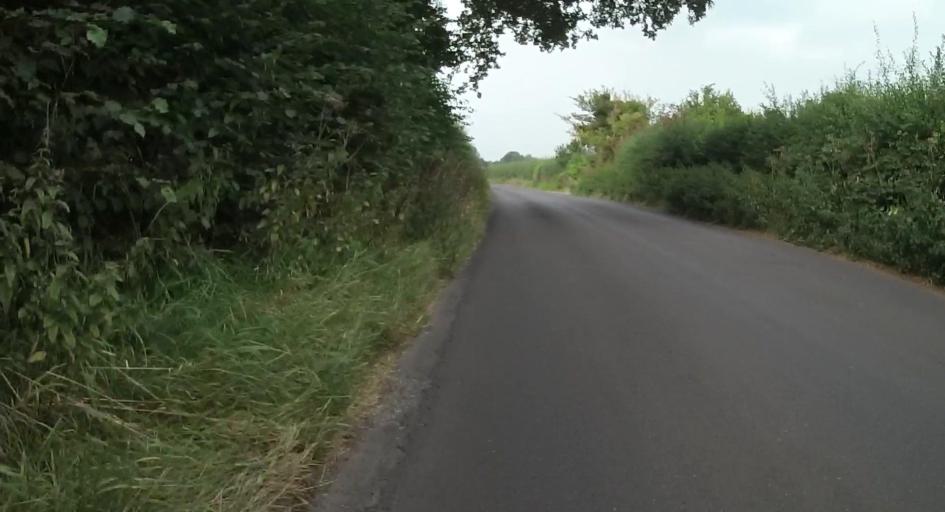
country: GB
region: England
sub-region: Hampshire
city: Old Basing
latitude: 51.2508
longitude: -1.0428
